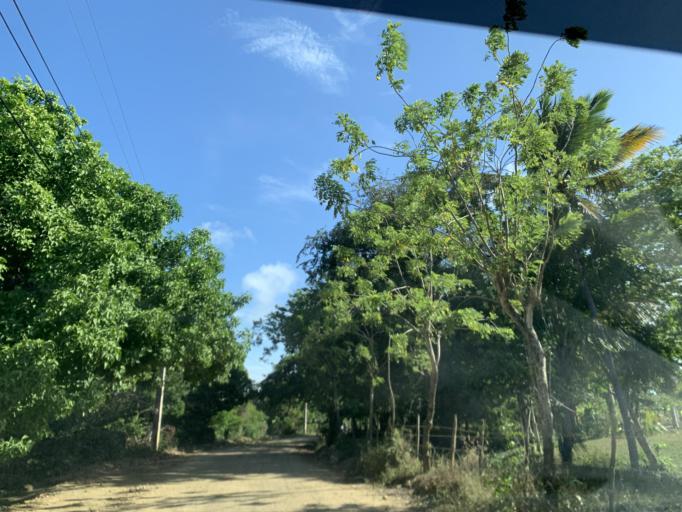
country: DO
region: Puerto Plata
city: Luperon
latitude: 19.8974
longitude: -70.8795
